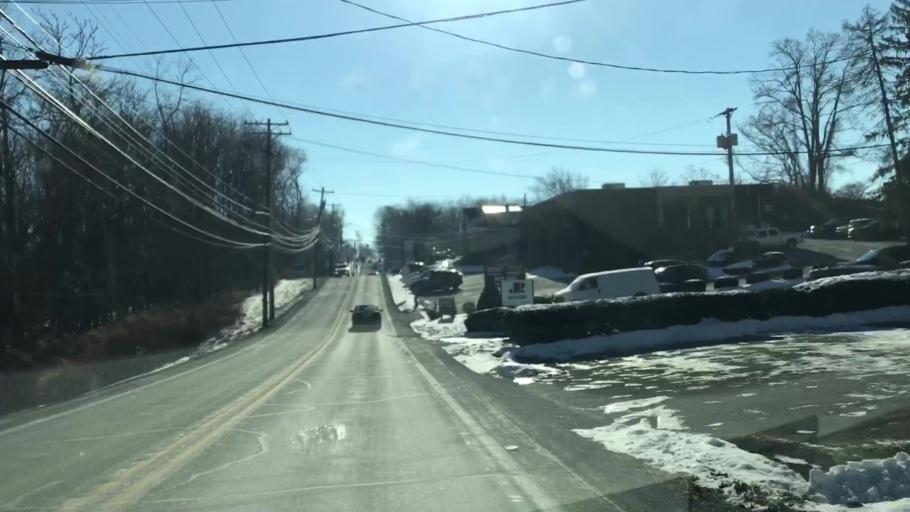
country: US
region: Pennsylvania
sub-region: Allegheny County
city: Carnot-Moon
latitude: 40.5137
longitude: -80.2168
